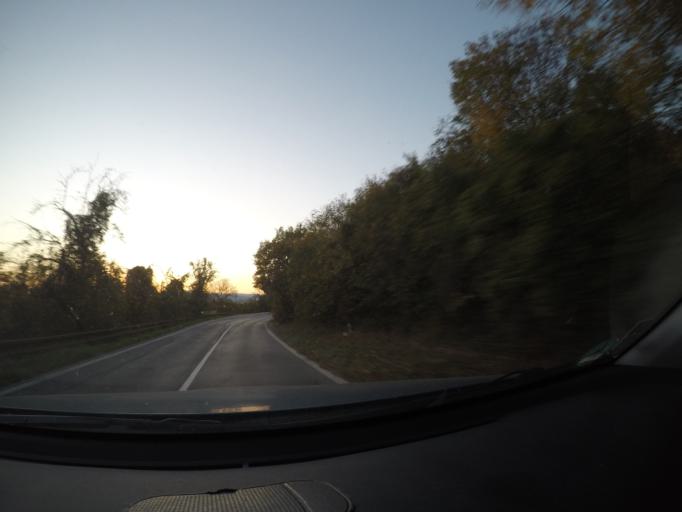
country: SK
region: Trenciansky
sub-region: Okres Trencin
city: Trencin
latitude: 48.9053
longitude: 18.0636
